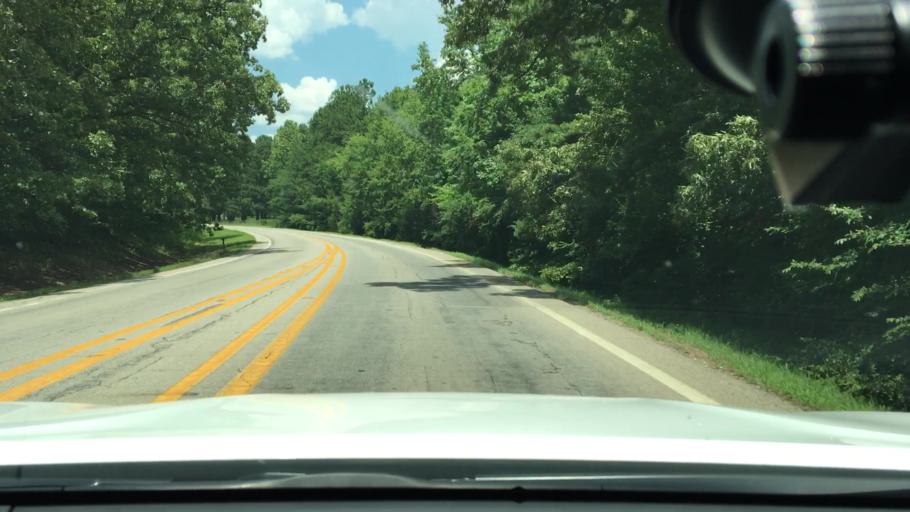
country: US
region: Arkansas
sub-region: Logan County
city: Booneville
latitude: 35.2097
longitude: -93.9256
